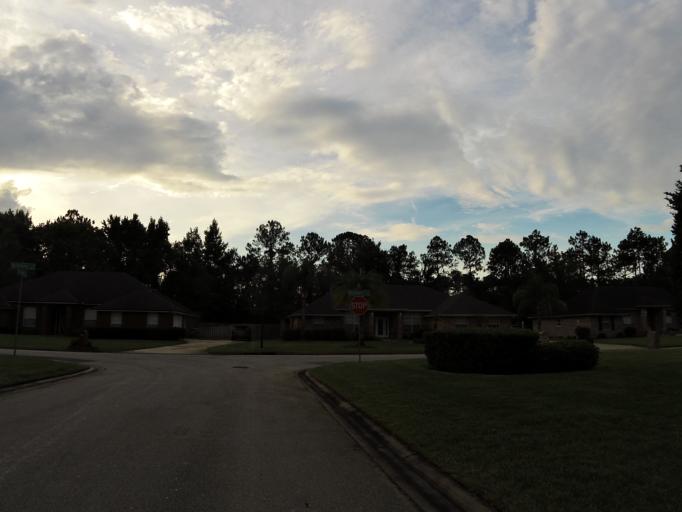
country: US
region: Florida
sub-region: Duval County
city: Baldwin
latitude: 30.3096
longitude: -81.8287
